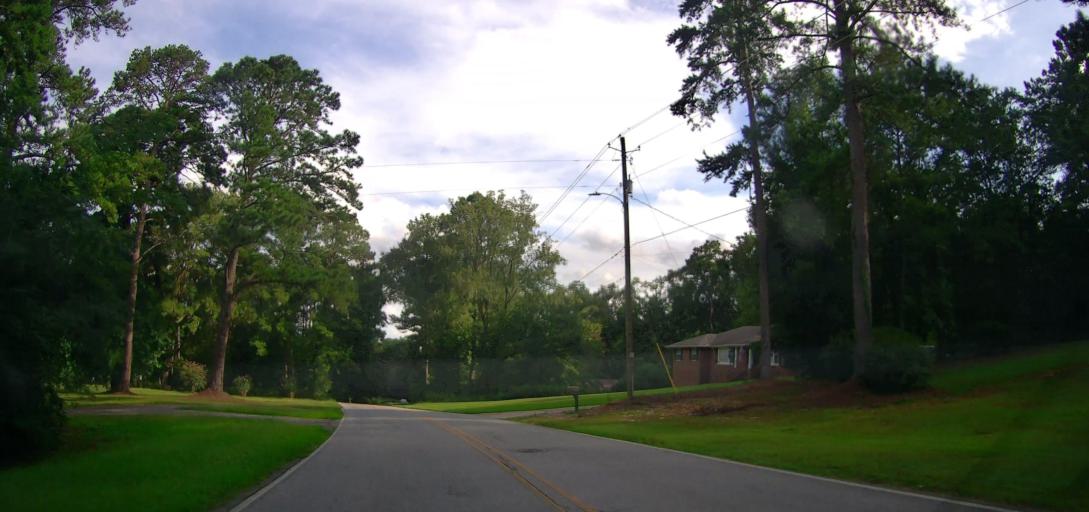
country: US
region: Alabama
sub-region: Russell County
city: Phenix City
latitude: 32.4972
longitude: -85.0012
